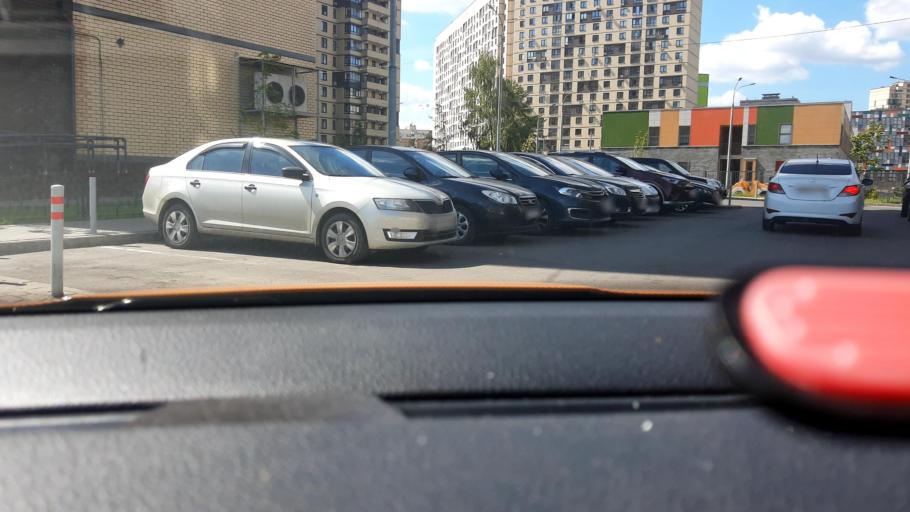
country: RU
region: Moskovskaya
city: Mytishchi
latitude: 55.9261
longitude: 37.7299
